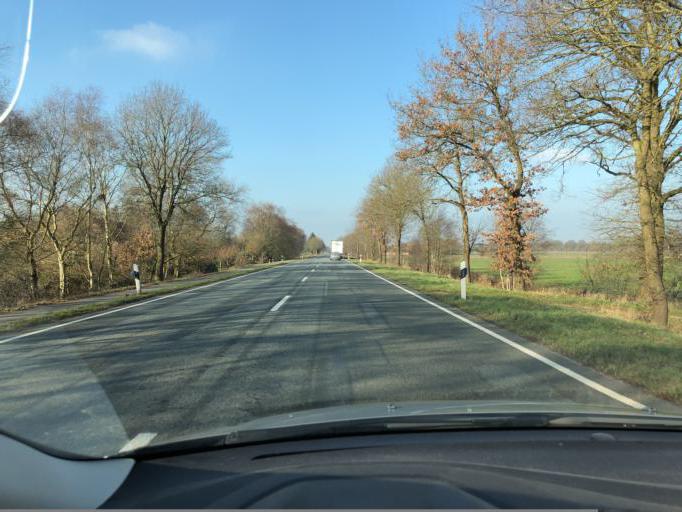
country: DE
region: Lower Saxony
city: Apen
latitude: 53.2958
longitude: 7.8272
